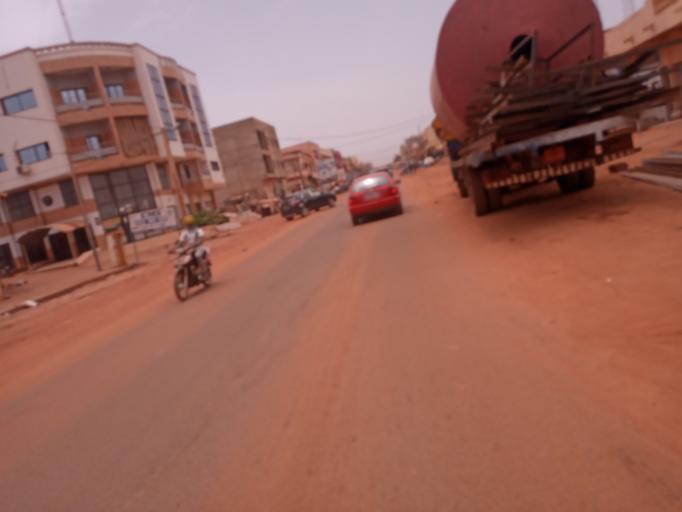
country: ML
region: Bamako
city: Bamako
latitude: 12.5810
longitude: -8.0191
